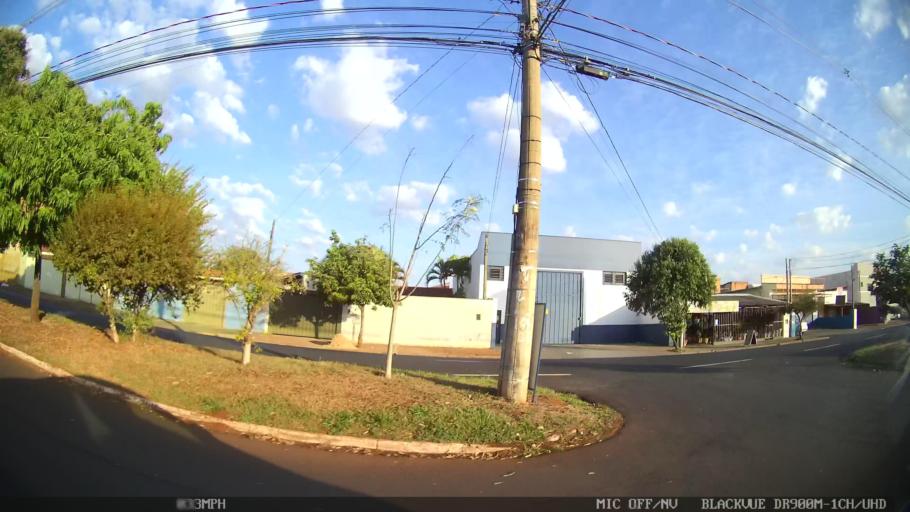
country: BR
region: Sao Paulo
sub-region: Ribeirao Preto
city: Ribeirao Preto
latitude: -21.1618
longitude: -47.7369
